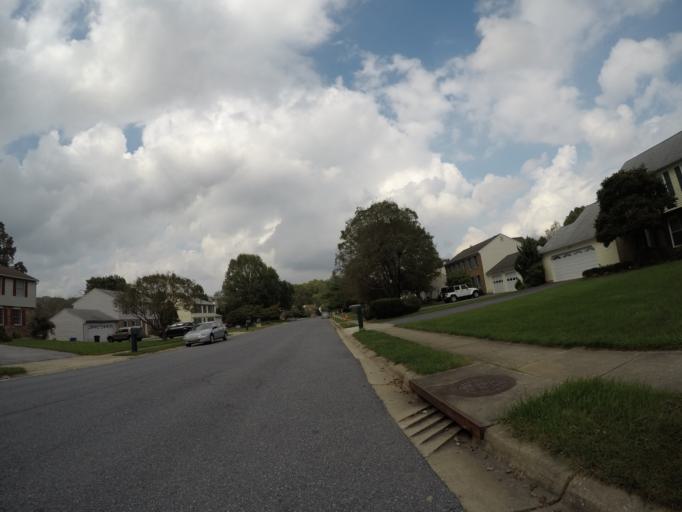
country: US
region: Maryland
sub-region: Howard County
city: Columbia
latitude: 39.2583
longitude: -76.8613
